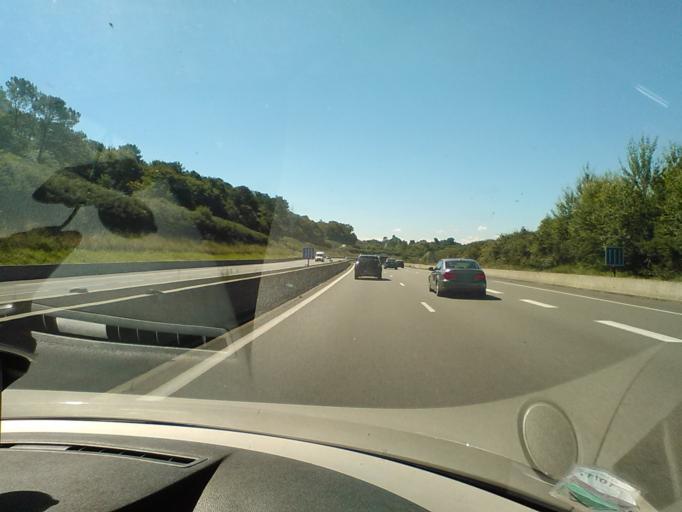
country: FR
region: Aquitaine
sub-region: Departement des Landes
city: Ondres
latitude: 43.5380
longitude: -1.4320
